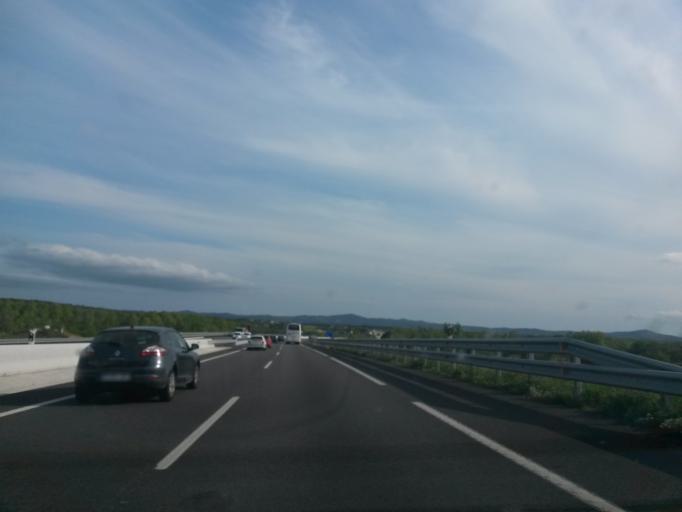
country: ES
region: Catalonia
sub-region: Provincia de Girona
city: Sils
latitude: 41.8200
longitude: 2.7632
